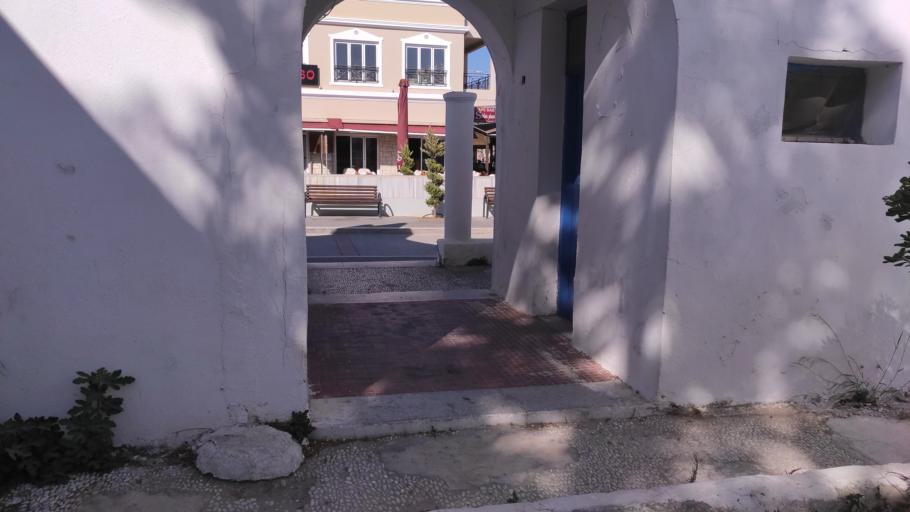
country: GR
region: South Aegean
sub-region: Nomos Dodekanisou
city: Kardamaina
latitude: 36.7820
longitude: 27.1438
